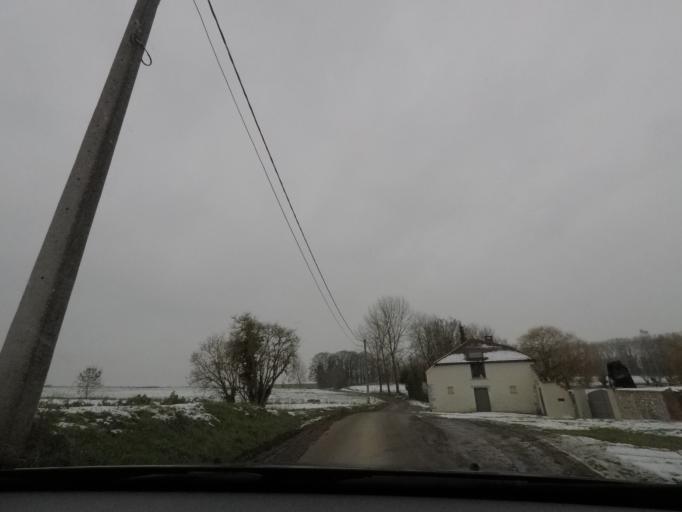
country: BE
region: Wallonia
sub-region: Province du Hainaut
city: Brugelette
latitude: 50.5925
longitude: 3.8842
